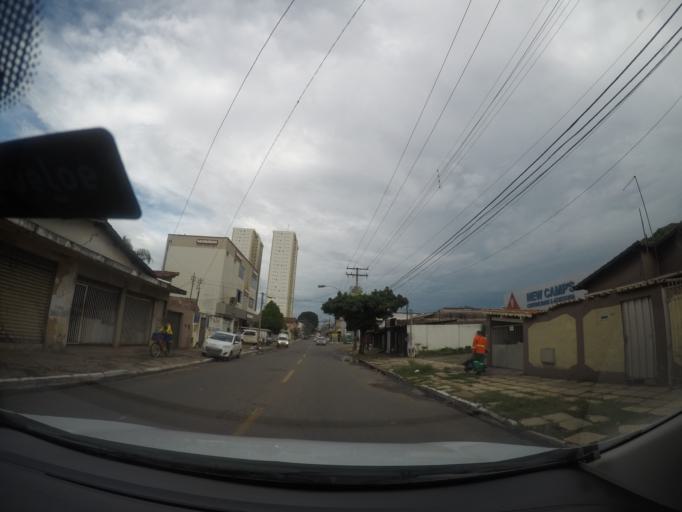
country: BR
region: Goias
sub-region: Goiania
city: Goiania
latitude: -16.6649
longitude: -49.2926
